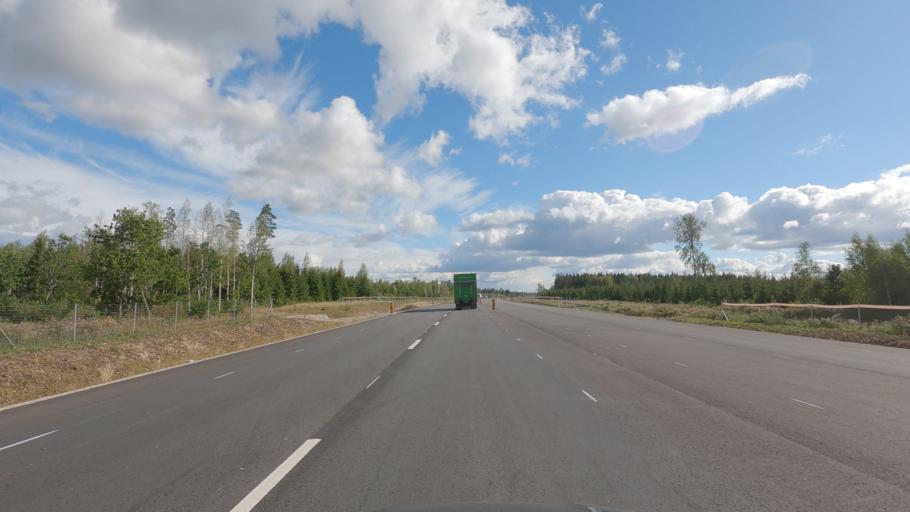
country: EE
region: Jaervamaa
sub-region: Paide linn
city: Paide
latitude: 58.9816
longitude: 25.6011
